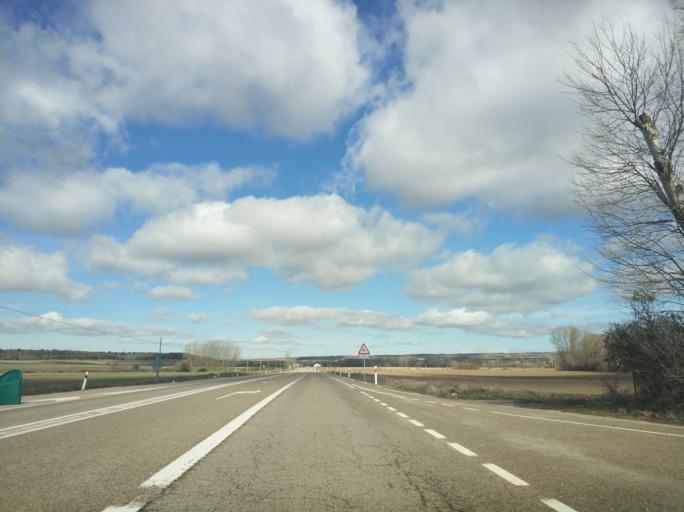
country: ES
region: Castille and Leon
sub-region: Provincia de Burgos
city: Revillarruz
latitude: 42.2365
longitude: -3.6687
